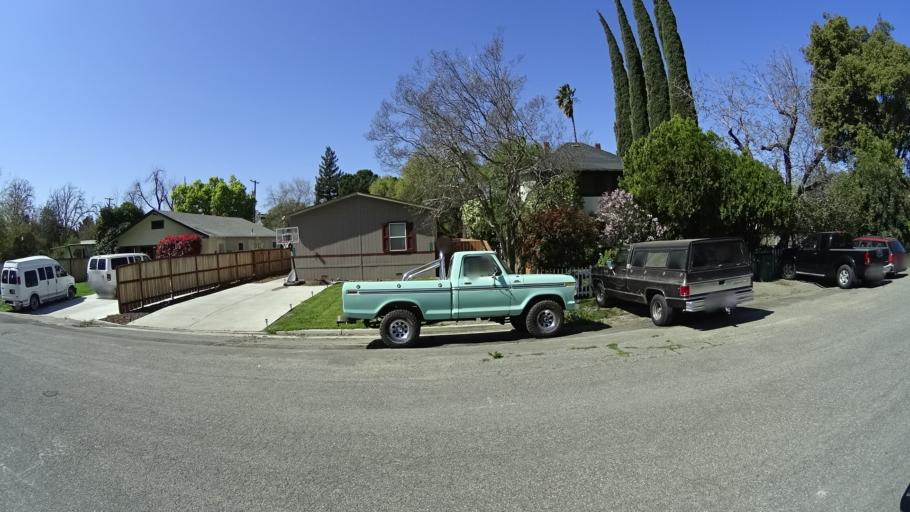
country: US
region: California
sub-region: Glenn County
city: Hamilton City
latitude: 39.7399
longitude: -122.0142
